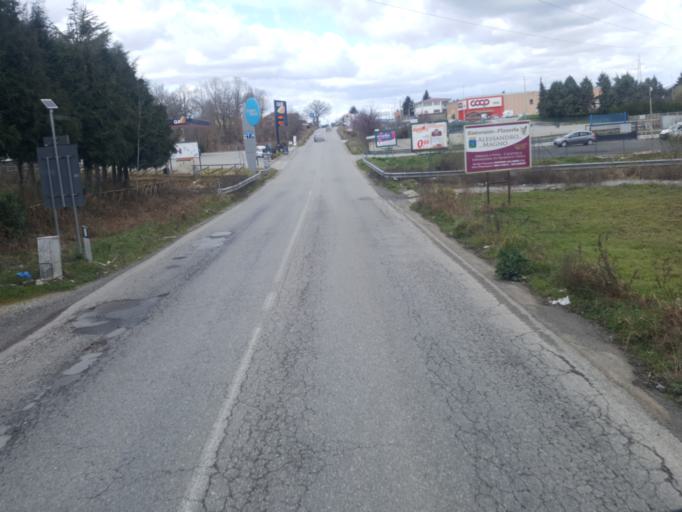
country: IT
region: Calabria
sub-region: Provincia di Cosenza
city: Santo Stefano di Rogliano
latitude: 39.2125
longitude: 16.3087
